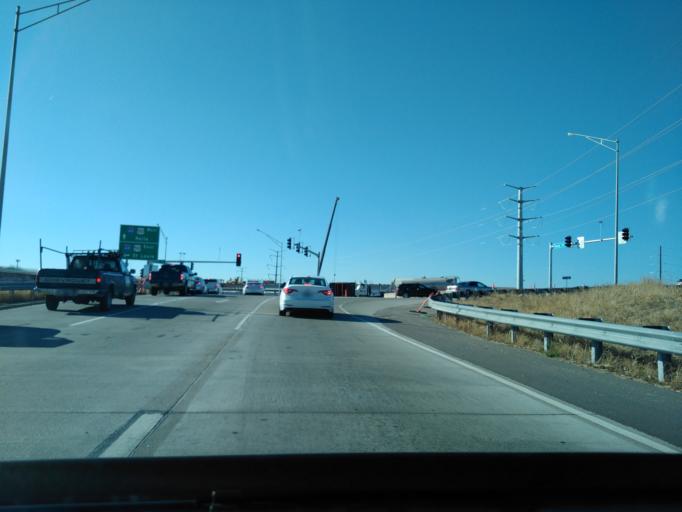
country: US
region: Missouri
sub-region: Saint Louis County
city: Valley Park
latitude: 38.5406
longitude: -90.4946
